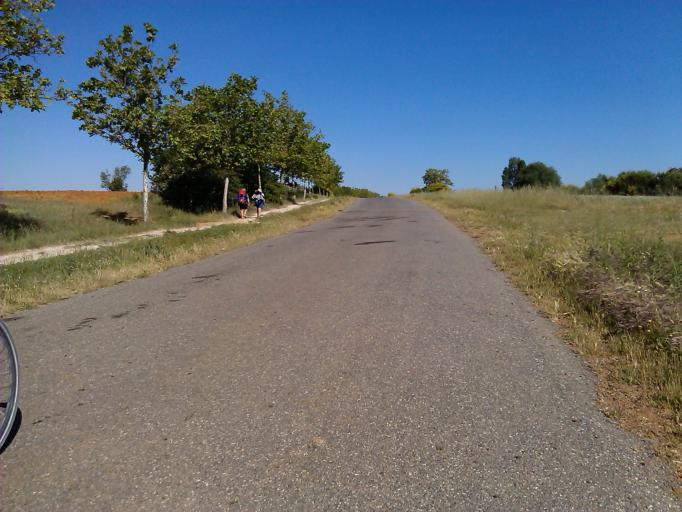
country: ES
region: Castille and Leon
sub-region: Provincia de Leon
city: Bercianos del Real Camino
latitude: 42.3903
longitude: -5.1488
